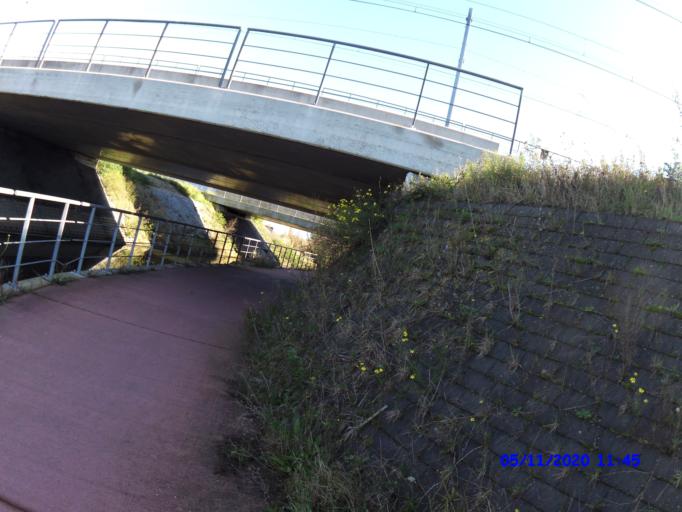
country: BE
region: Flanders
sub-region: Provincie West-Vlaanderen
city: Brugge
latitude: 51.2450
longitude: 3.2070
